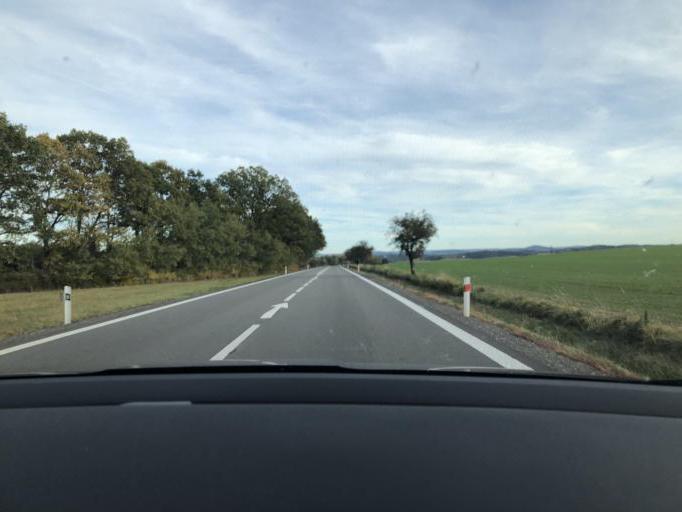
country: CZ
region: Central Bohemia
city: Postupice
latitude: 49.7530
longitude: 14.7688
